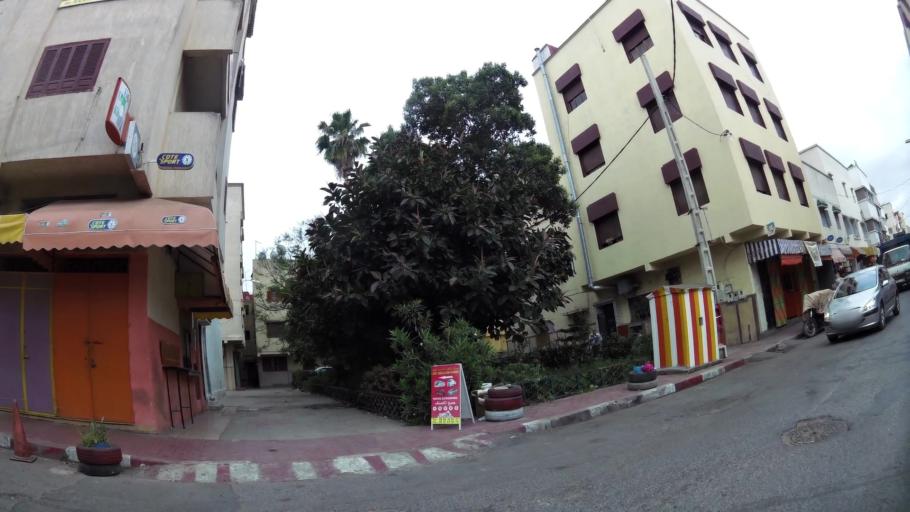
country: MA
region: Rabat-Sale-Zemmour-Zaer
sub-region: Rabat
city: Rabat
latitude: 33.9851
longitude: -6.8222
